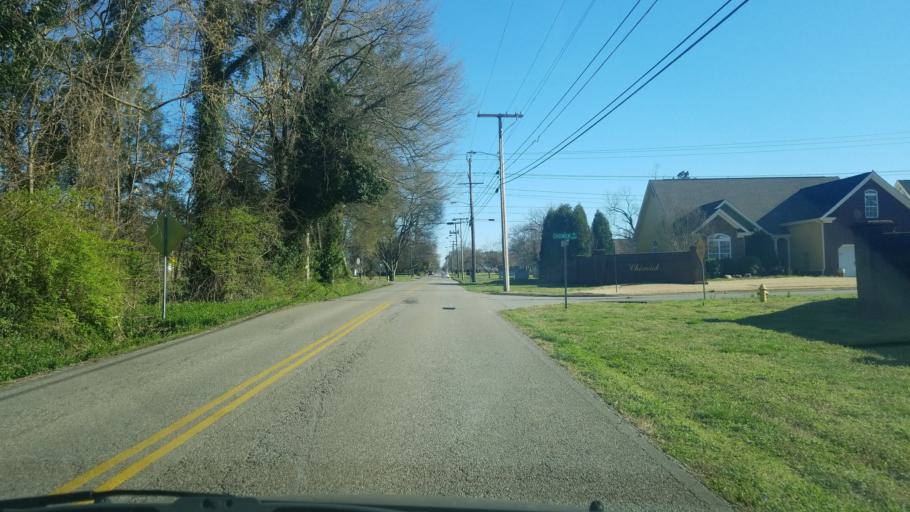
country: US
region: Tennessee
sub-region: Hamilton County
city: East Brainerd
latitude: 35.0319
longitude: -85.1740
